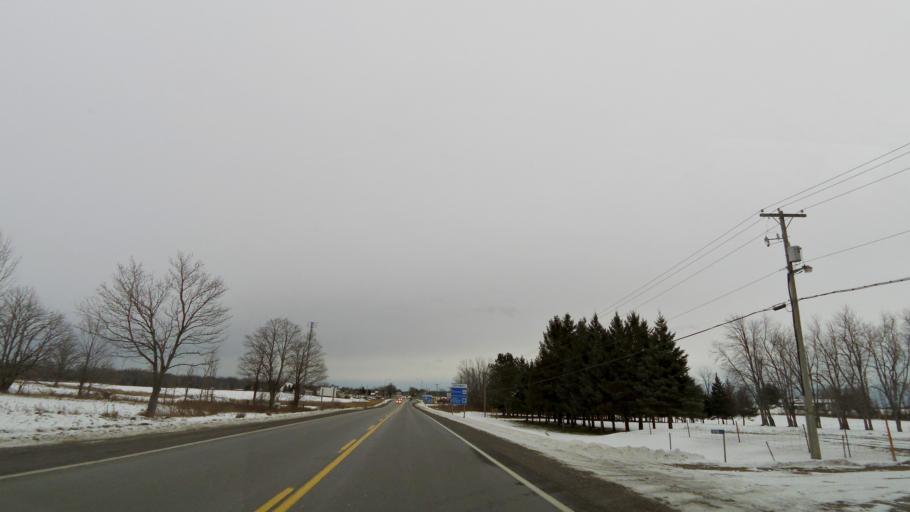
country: CA
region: Ontario
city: Ancaster
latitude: 43.2838
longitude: -80.0752
